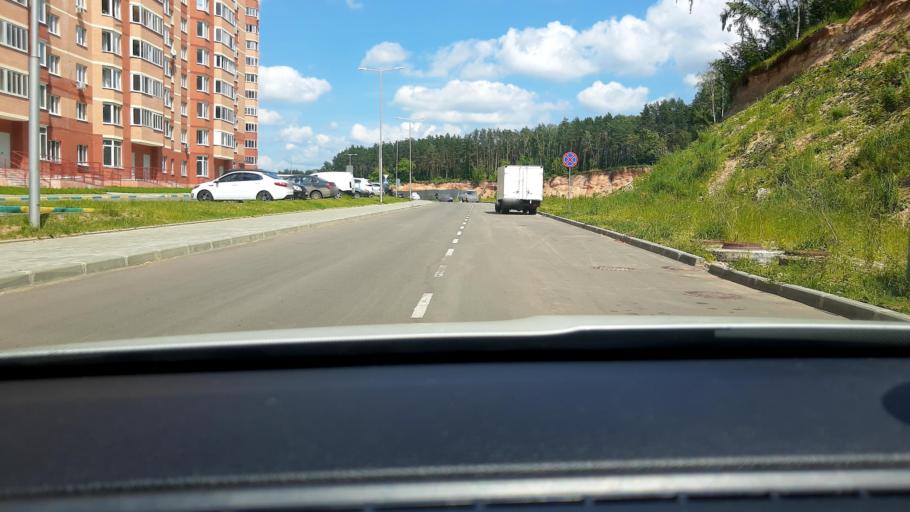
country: RU
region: Moskovskaya
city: Dzerzhinskiy
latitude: 55.6421
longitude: 37.8592
